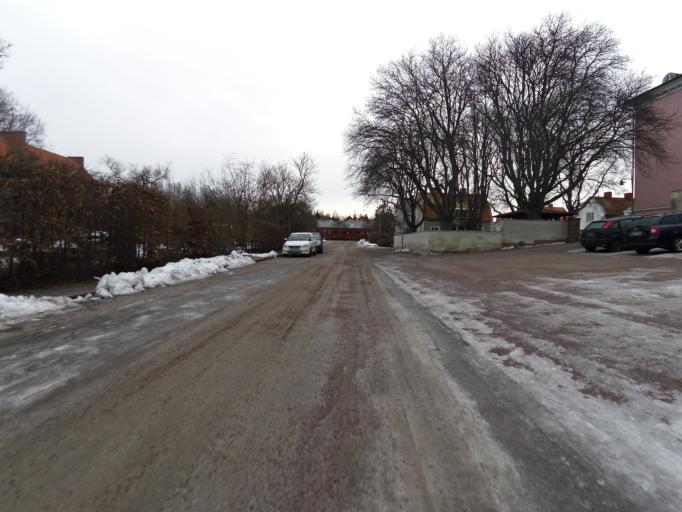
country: SE
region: Gaevleborg
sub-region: Gavle Kommun
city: Gavle
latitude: 60.6674
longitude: 17.1401
